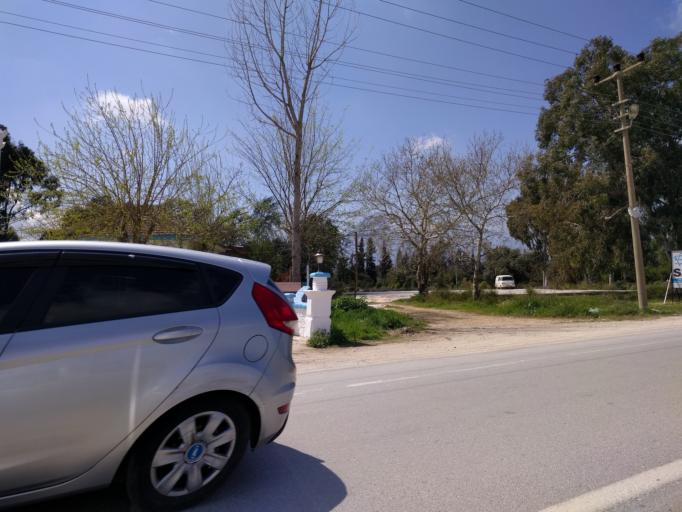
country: TR
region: Antalya
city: Cakirlar
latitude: 36.8934
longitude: 30.6010
